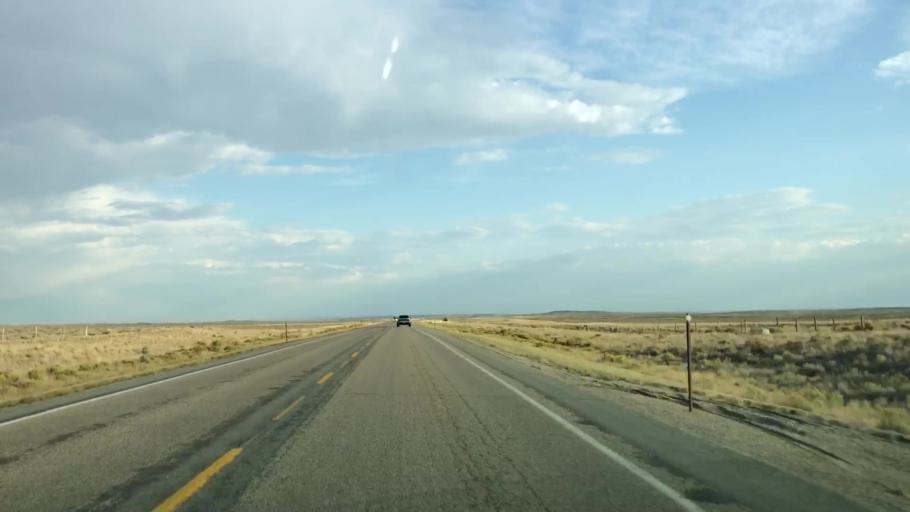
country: US
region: Wyoming
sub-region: Sublette County
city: Pinedale
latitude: 42.4051
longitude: -109.5490
